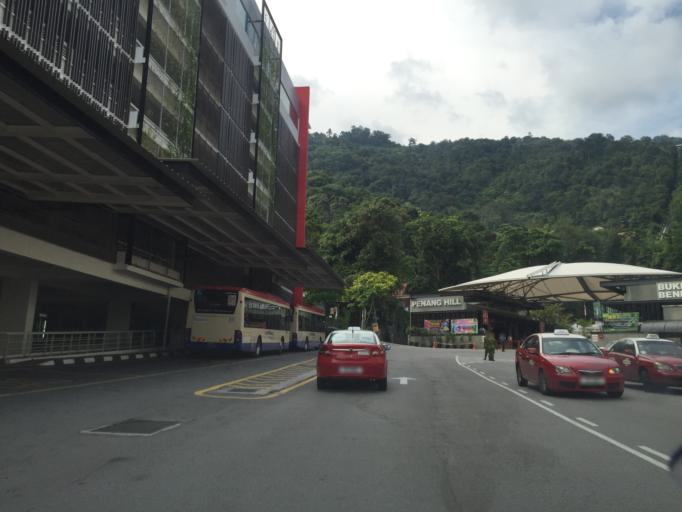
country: MY
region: Penang
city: George Town
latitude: 5.4077
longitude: 100.2777
